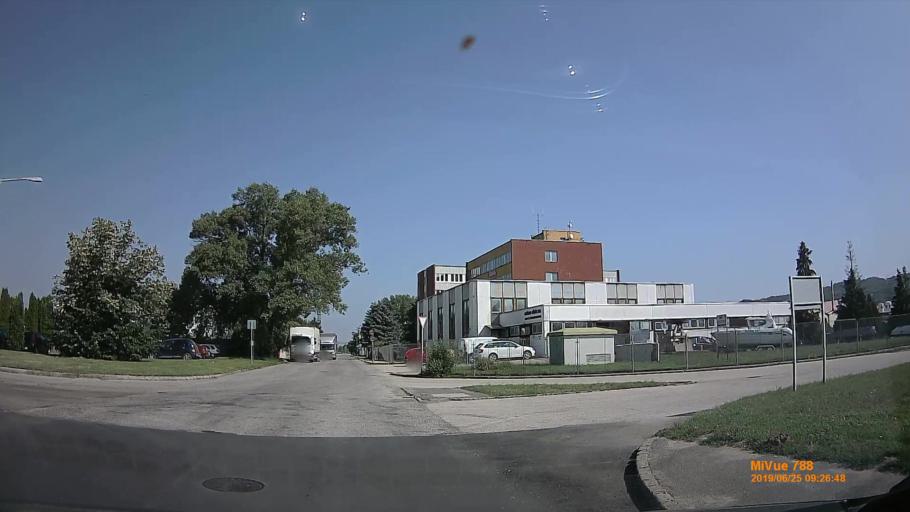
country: HU
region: Komarom-Esztergom
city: Esztergom
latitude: 47.7703
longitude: 18.7460
